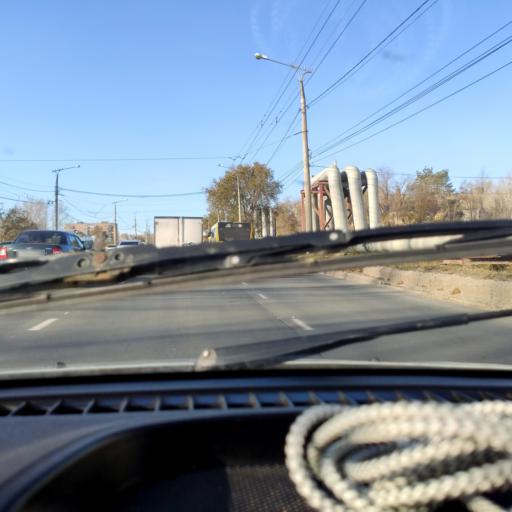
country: RU
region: Samara
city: Zhigulevsk
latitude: 53.4876
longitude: 49.4930
